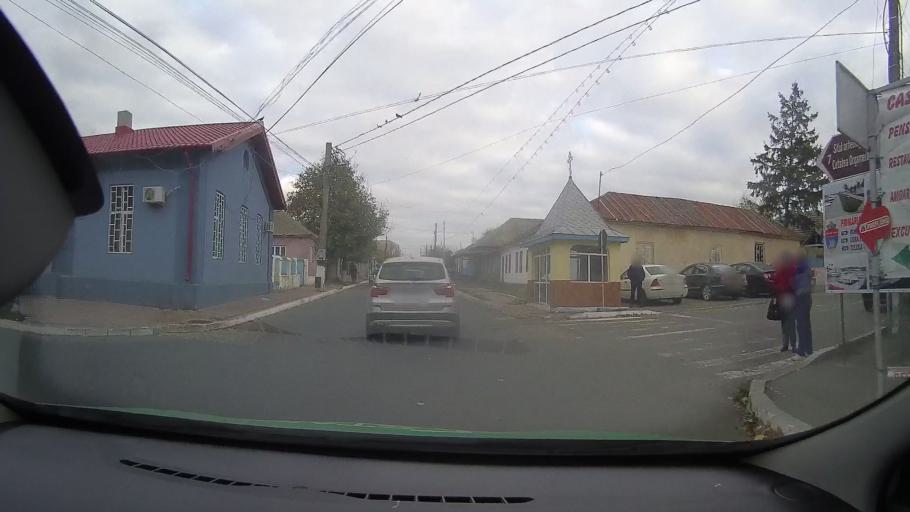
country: RO
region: Tulcea
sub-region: Comuna Jurilovca
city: Jurilovca
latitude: 44.7587
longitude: 28.8757
